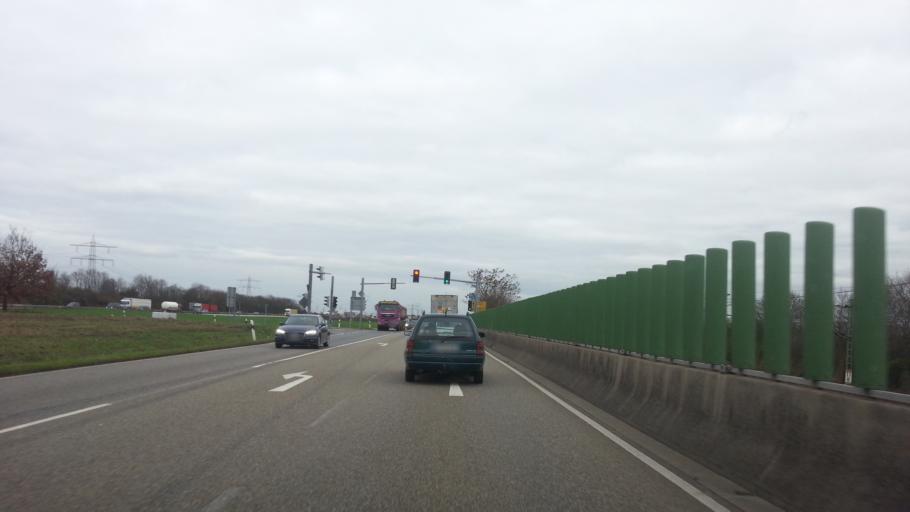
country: DE
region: Baden-Wuerttemberg
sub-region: Karlsruhe Region
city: Bruhl
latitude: 49.3966
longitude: 8.5455
